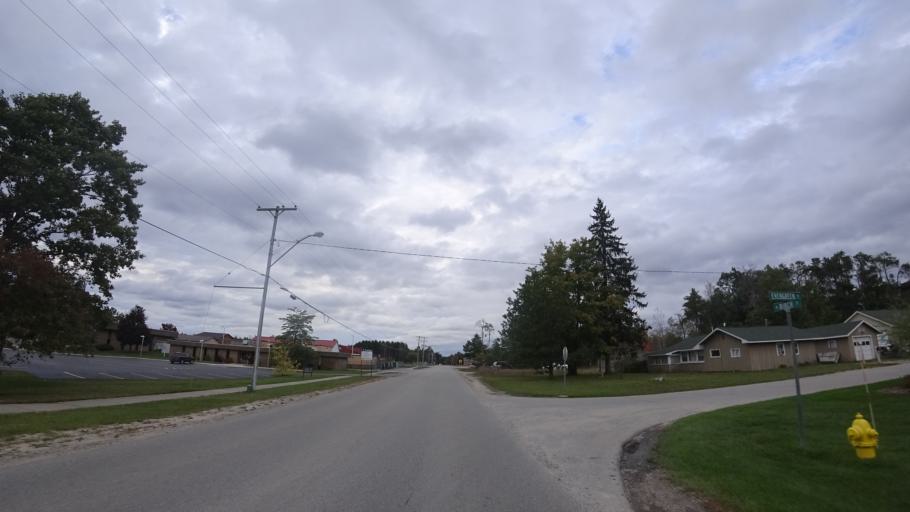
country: US
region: Michigan
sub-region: Kalkaska County
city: Kalkaska
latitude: 44.7399
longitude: -85.1845
